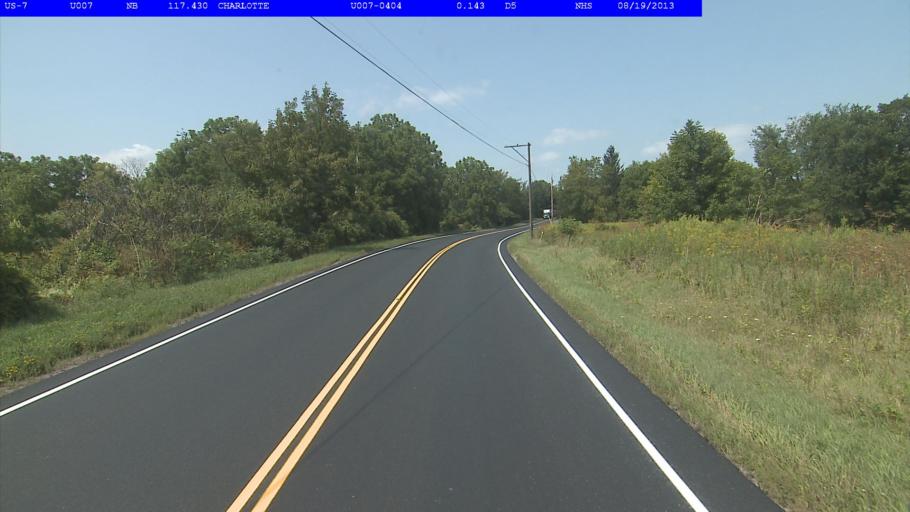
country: US
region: Vermont
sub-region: Addison County
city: Vergennes
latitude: 44.2644
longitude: -73.2316
